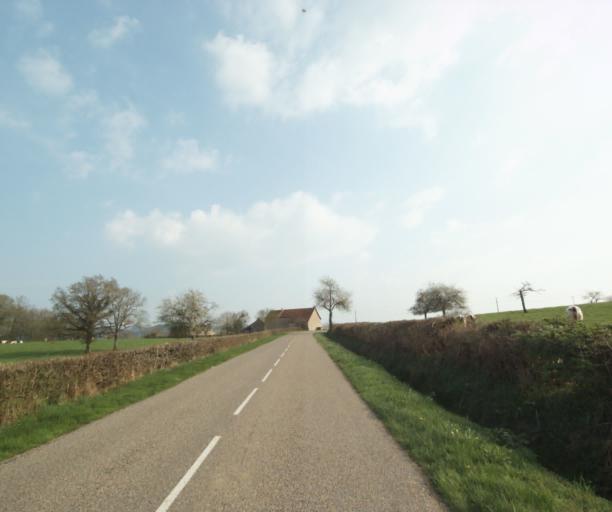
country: FR
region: Bourgogne
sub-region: Departement de Saone-et-Loire
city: Charolles
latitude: 46.4613
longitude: 4.4400
